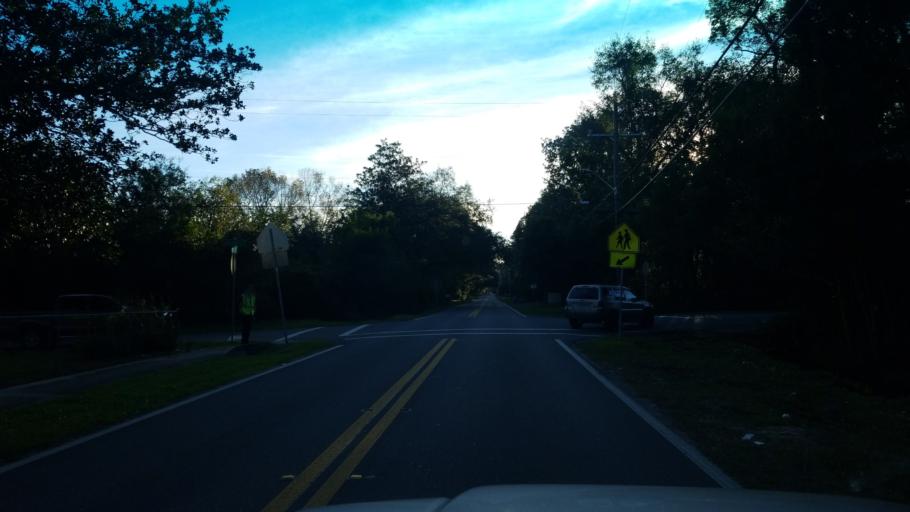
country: US
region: Florida
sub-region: Duval County
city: Jacksonville
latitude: 30.3294
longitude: -81.7863
